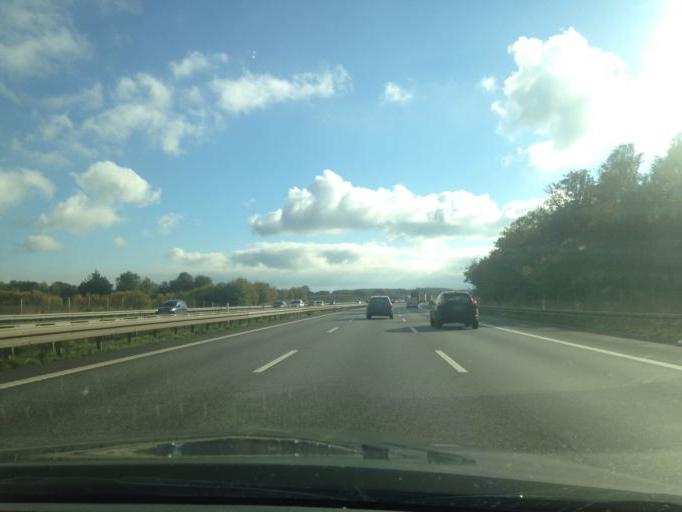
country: DK
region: South Denmark
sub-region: Vejle Kommune
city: Vejle
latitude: 55.6549
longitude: 9.5605
